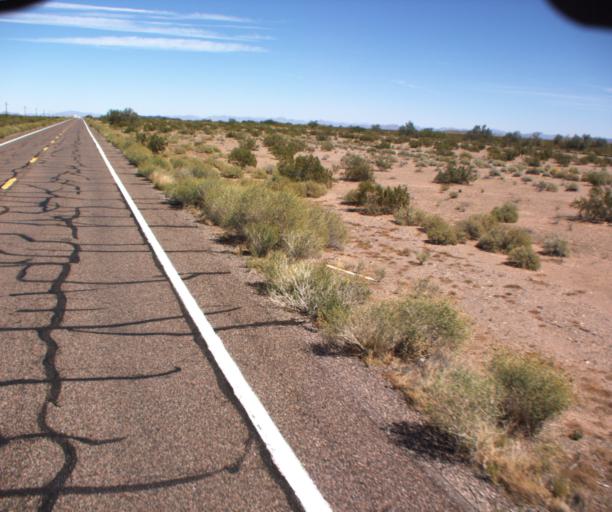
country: US
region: Arizona
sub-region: Maricopa County
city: Gila Bend
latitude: 32.7600
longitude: -112.8219
